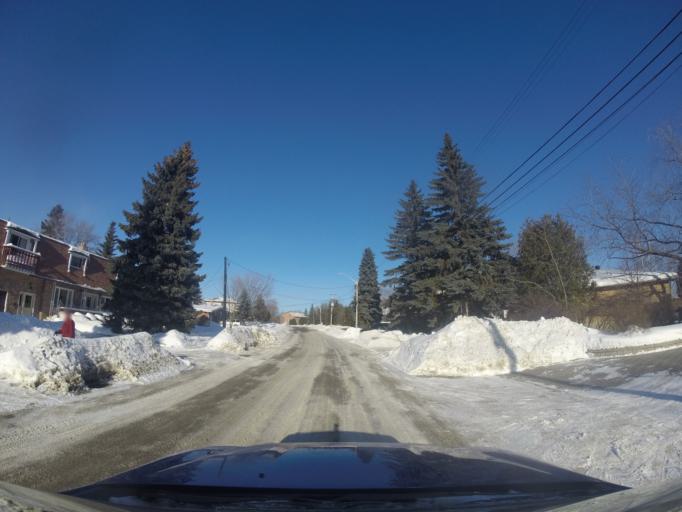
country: CA
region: Ontario
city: Greater Sudbury
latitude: 46.4629
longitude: -80.9902
